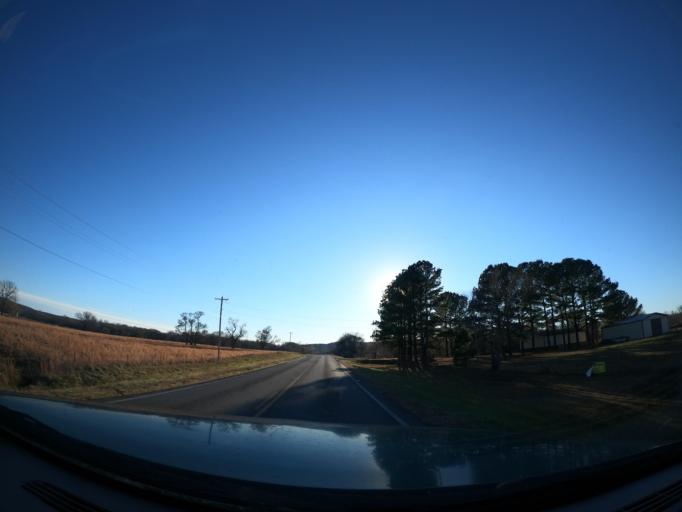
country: US
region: Oklahoma
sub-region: Latimer County
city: Wilburton
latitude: 34.8995
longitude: -95.4334
